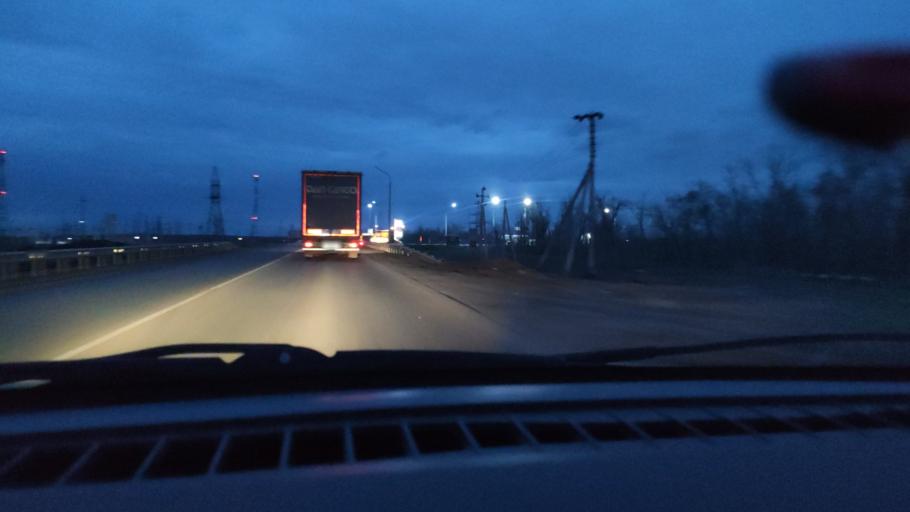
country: RU
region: Orenburg
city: Tatarskaya Kargala
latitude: 51.9736
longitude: 55.1863
